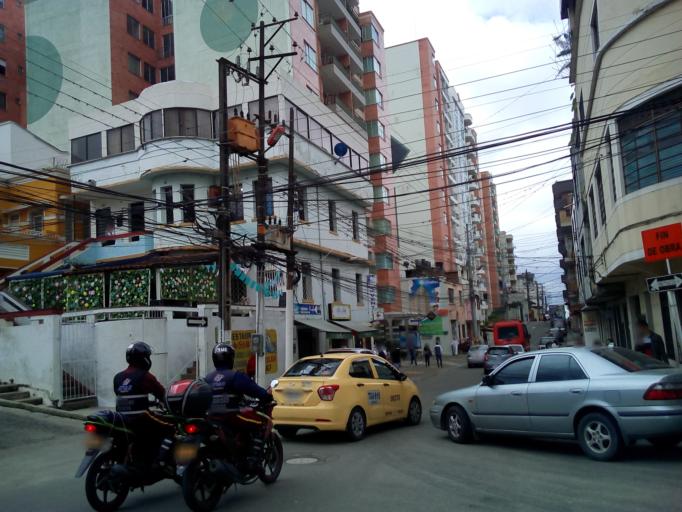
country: CO
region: Tolima
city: Ibague
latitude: 4.4467
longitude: -75.2435
